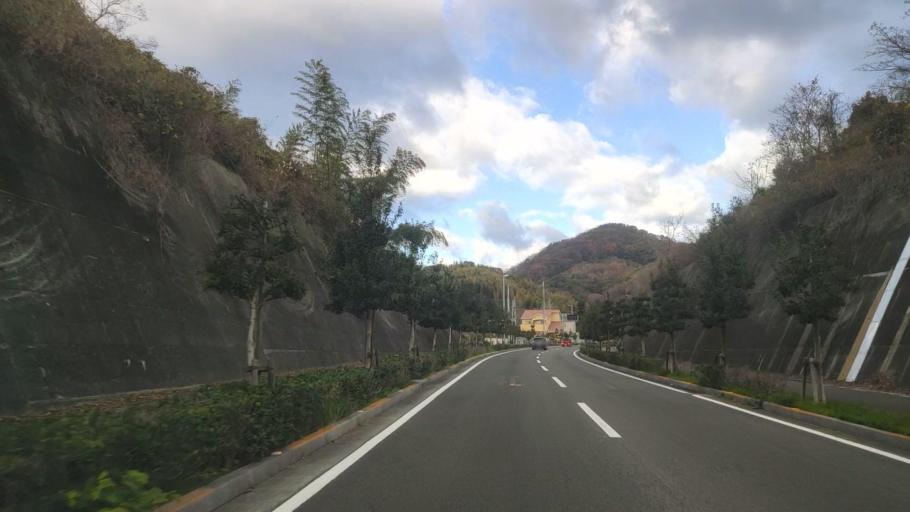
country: JP
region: Ehime
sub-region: Shikoku-chuo Shi
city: Matsuyama
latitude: 33.8742
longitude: 132.7162
